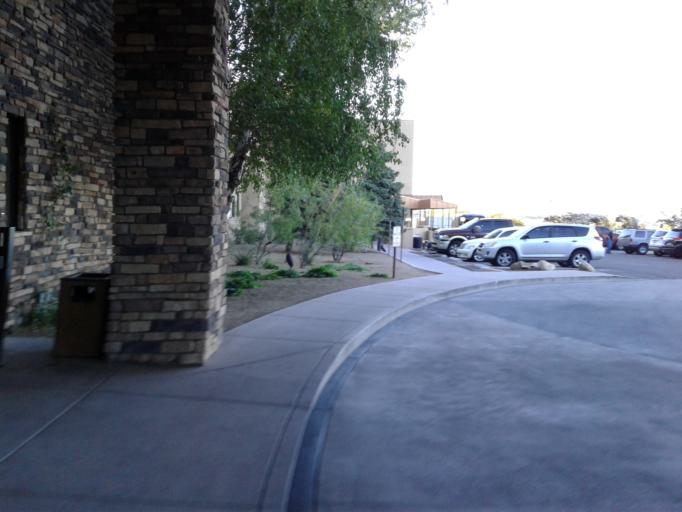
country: US
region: Arizona
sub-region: Yavapai County
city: Prescott
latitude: 34.5509
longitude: -112.4469
